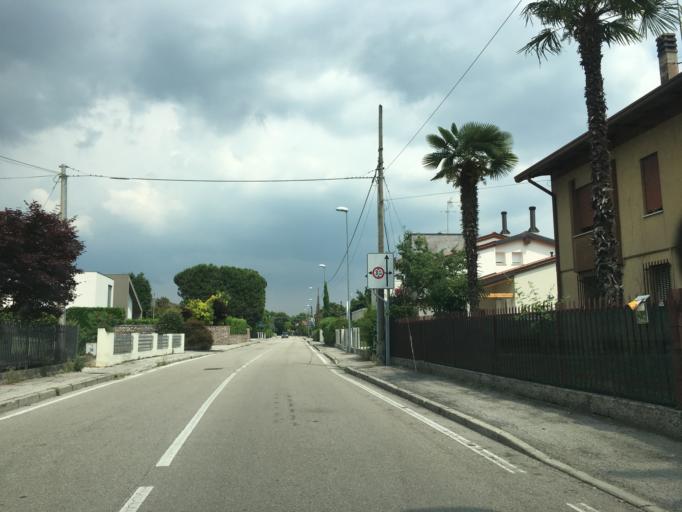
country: IT
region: Veneto
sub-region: Provincia di Padova
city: Galliera Veneta
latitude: 45.6648
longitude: 11.8277
